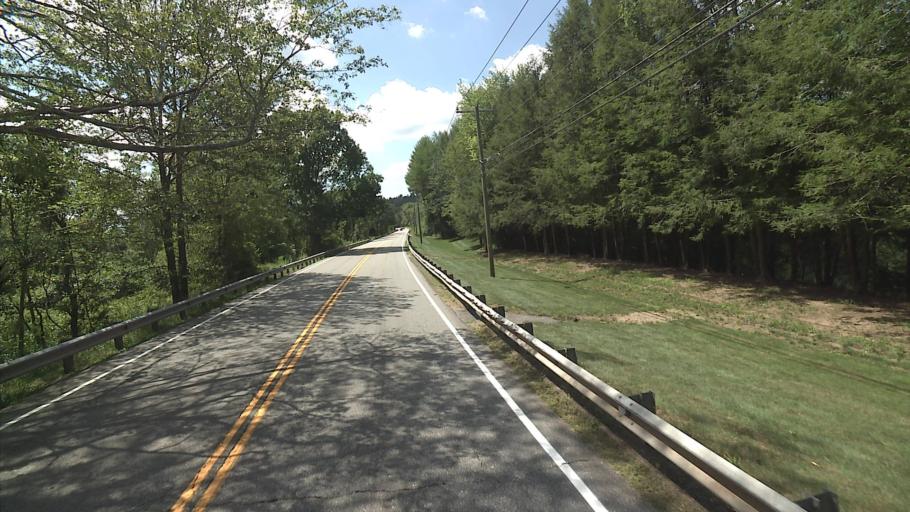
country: US
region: Connecticut
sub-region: Windham County
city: South Woodstock
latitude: 41.8695
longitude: -72.0902
